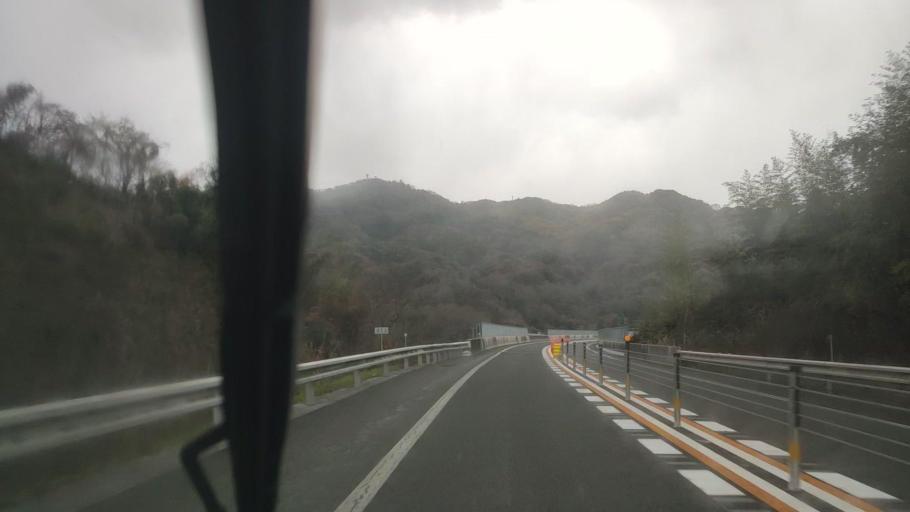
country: JP
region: Hiroshima
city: Innoshima
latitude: 34.1640
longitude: 133.0651
